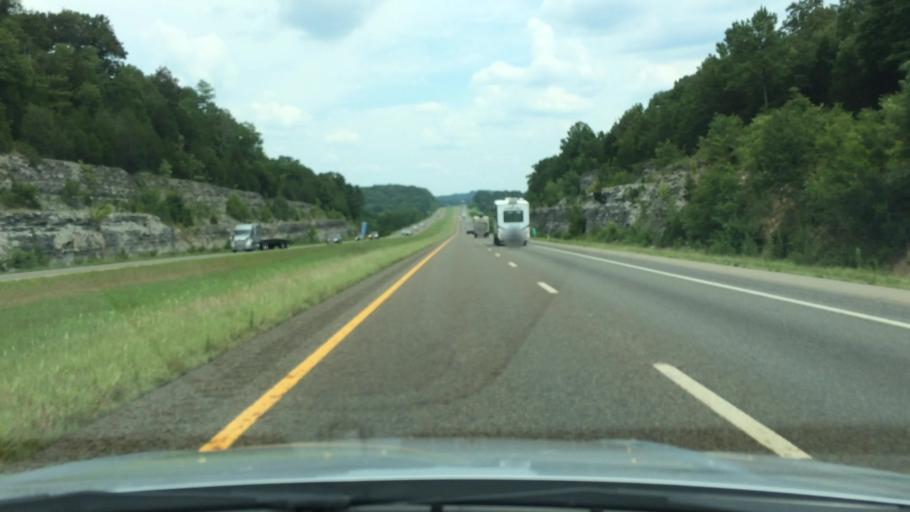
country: US
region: Tennessee
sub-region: Maury County
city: Columbia
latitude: 35.5972
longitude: -86.9018
